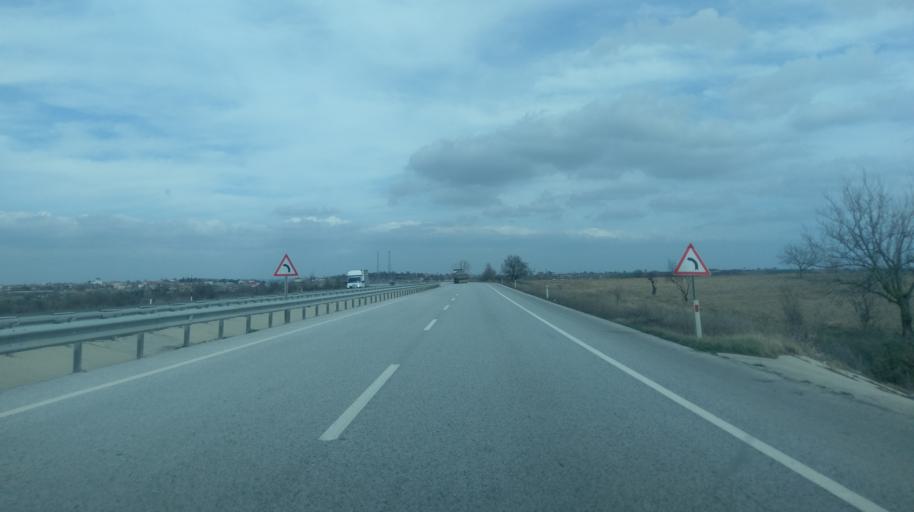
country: TR
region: Edirne
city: Kircasalih
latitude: 41.3804
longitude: 26.7871
